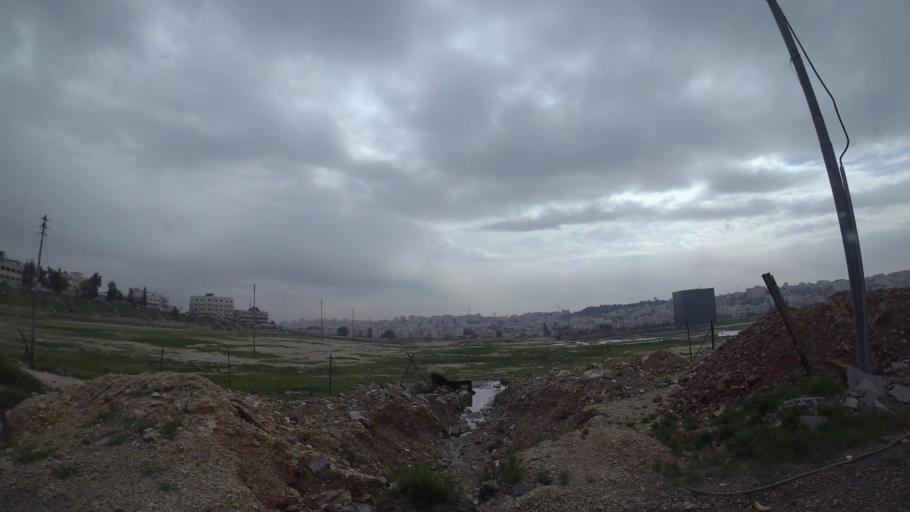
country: JO
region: Amman
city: Umm as Summaq
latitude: 31.9016
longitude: 35.8479
